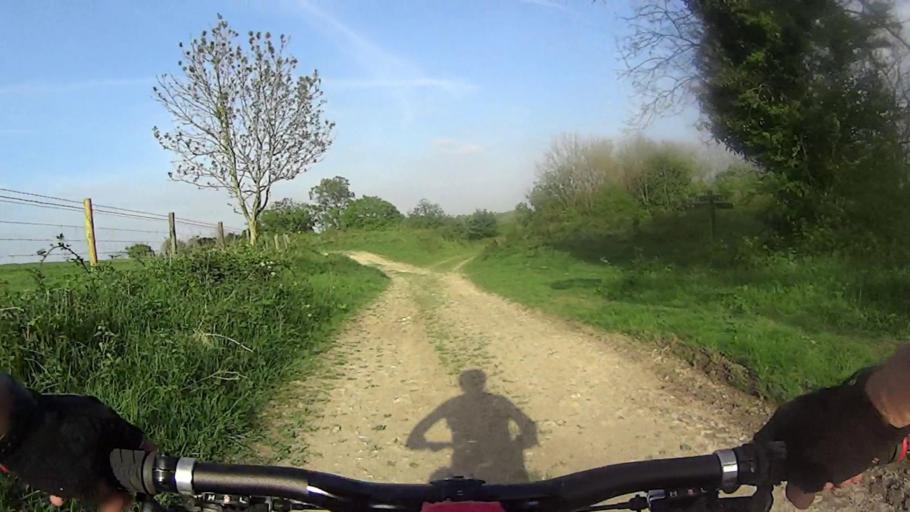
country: GB
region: England
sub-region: West Sussex
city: Fontwell
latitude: 50.9067
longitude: -0.6223
